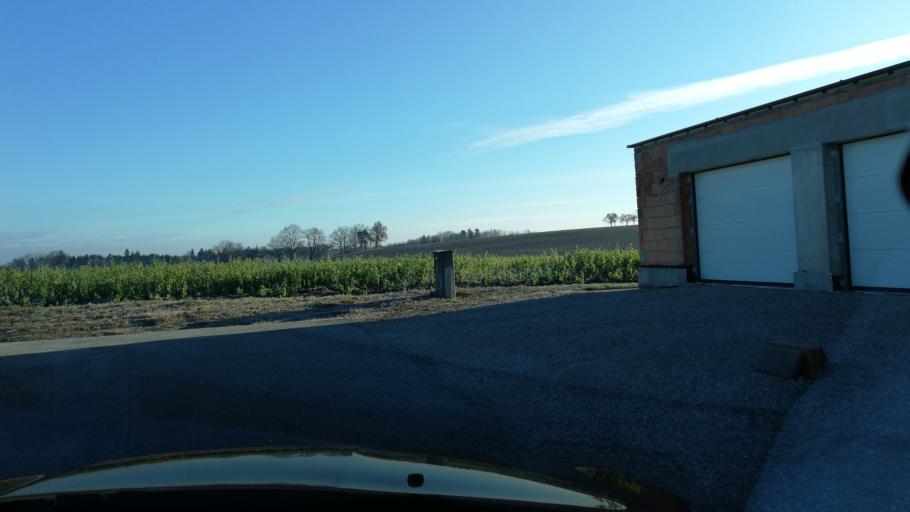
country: AT
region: Upper Austria
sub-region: Politischer Bezirk Steyr-Land
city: Bad Hall
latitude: 48.0355
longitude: 14.2173
